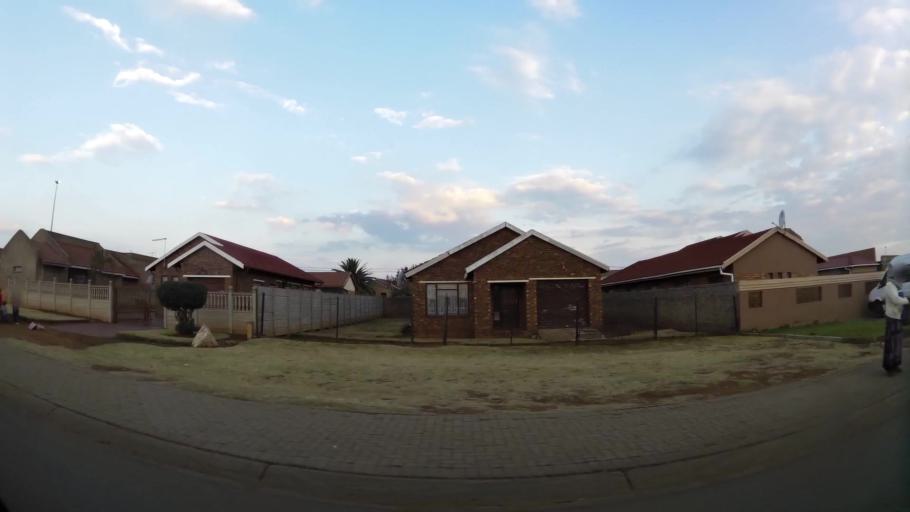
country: ZA
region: Gauteng
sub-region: City of Johannesburg Metropolitan Municipality
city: Orange Farm
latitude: -26.5622
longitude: 27.8530
